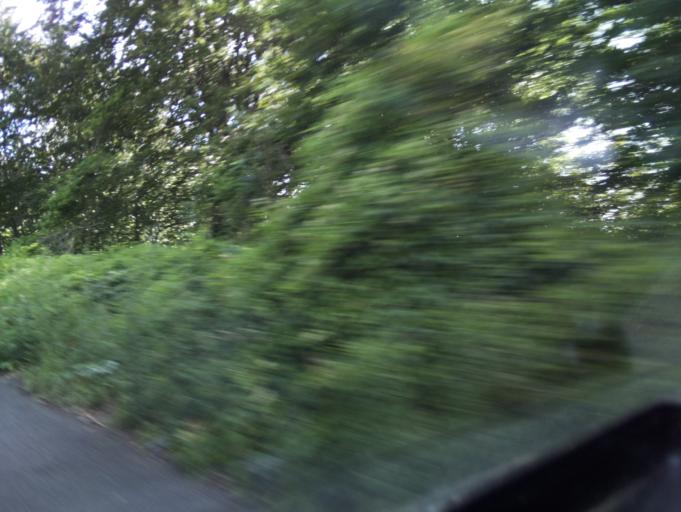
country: GB
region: England
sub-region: Gloucestershire
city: Cirencester
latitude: 51.7450
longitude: -1.9951
